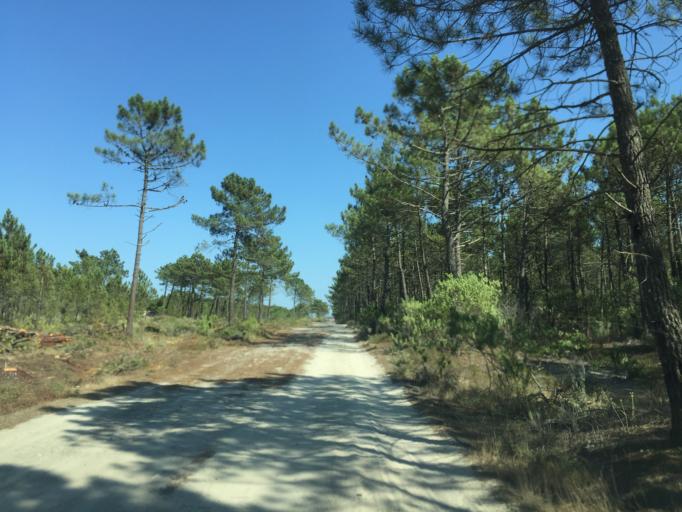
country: PT
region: Coimbra
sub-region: Figueira da Foz
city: Tavarede
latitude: 40.2593
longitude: -8.8465
